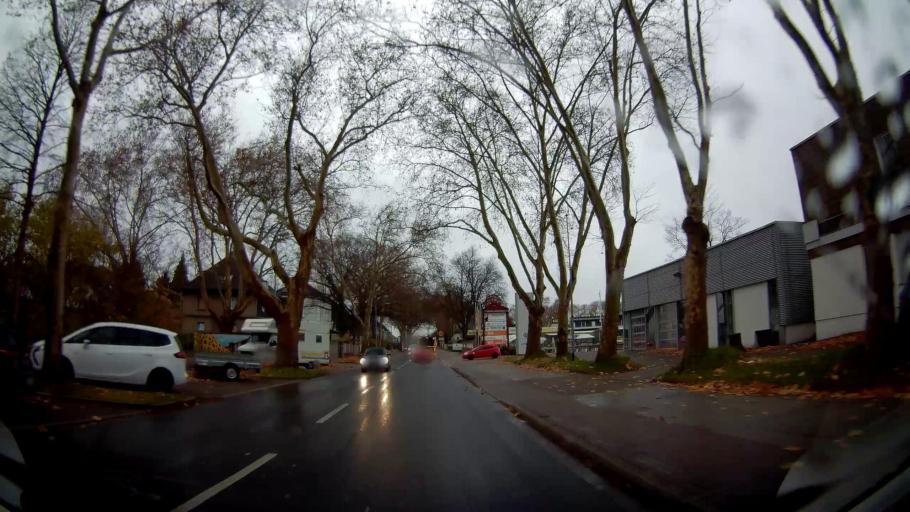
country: DE
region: North Rhine-Westphalia
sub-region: Regierungsbezirk Munster
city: Gelsenkirchen
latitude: 51.4728
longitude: 7.0824
